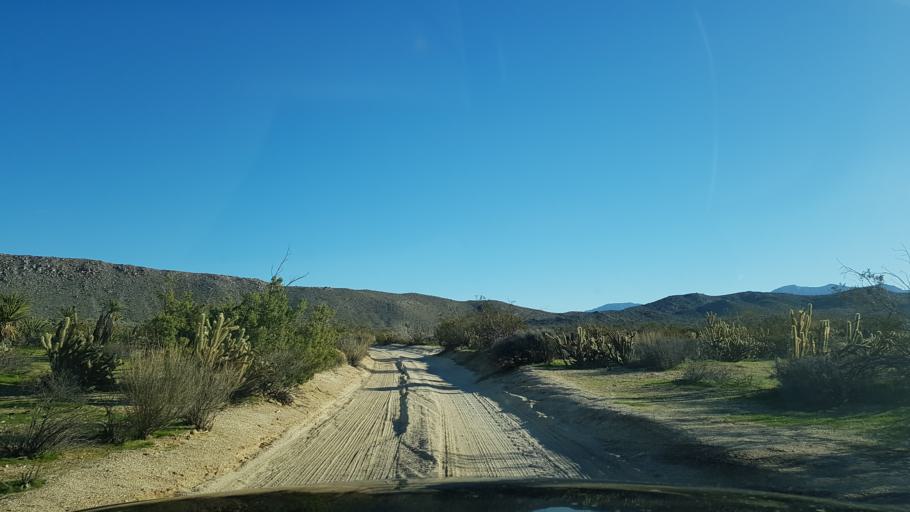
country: US
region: California
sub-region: San Diego County
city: Julian
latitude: 33.0127
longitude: -116.3965
